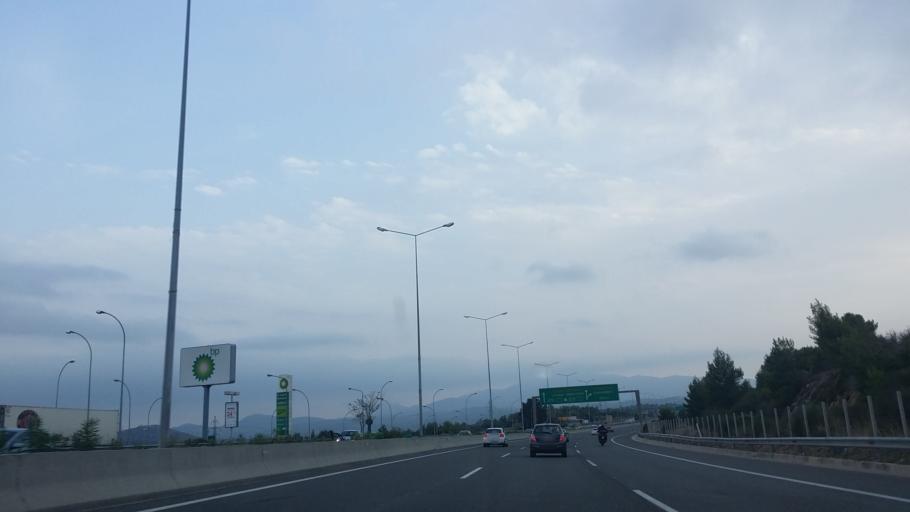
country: GR
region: Attica
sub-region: Nomarchia Anatolikis Attikis
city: Polydendri
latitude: 38.2125
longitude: 23.8548
